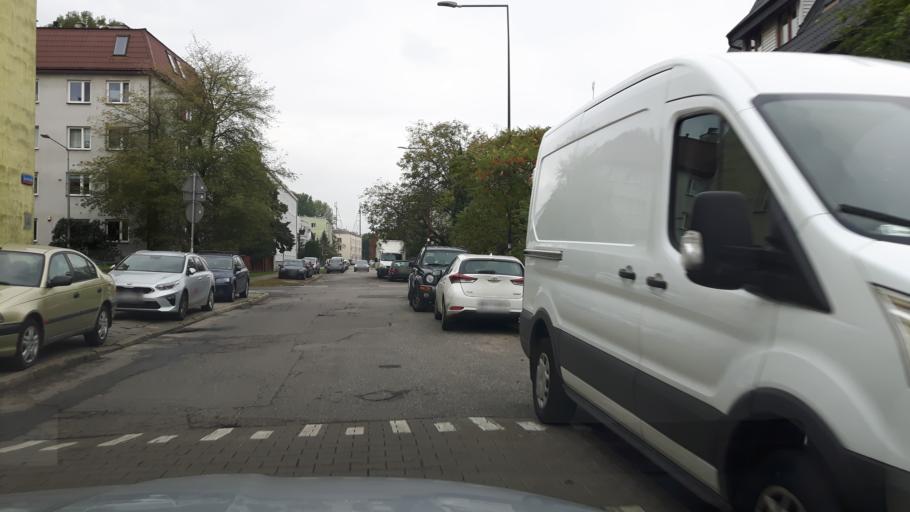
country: PL
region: Masovian Voivodeship
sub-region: Warszawa
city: Praga Poludnie
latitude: 52.2482
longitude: 21.1035
